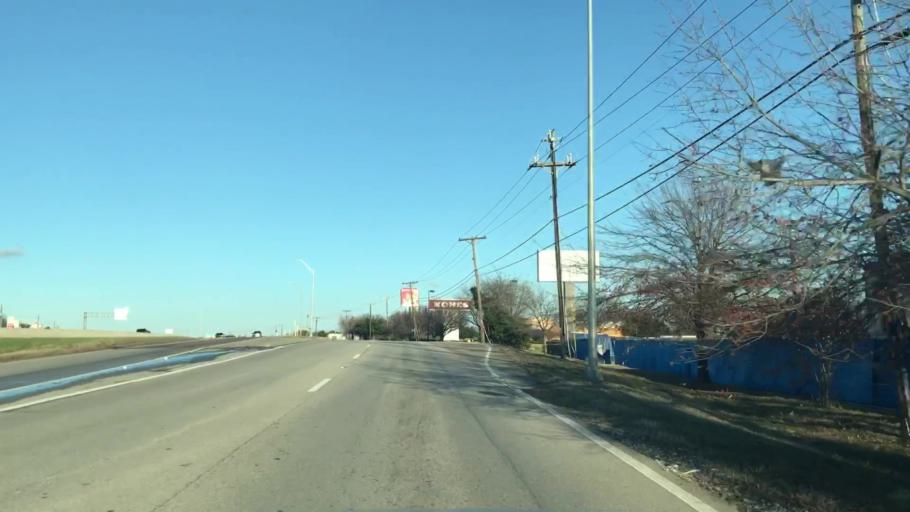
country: US
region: Texas
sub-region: Rockwall County
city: Rockwall
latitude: 32.8996
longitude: -96.4601
